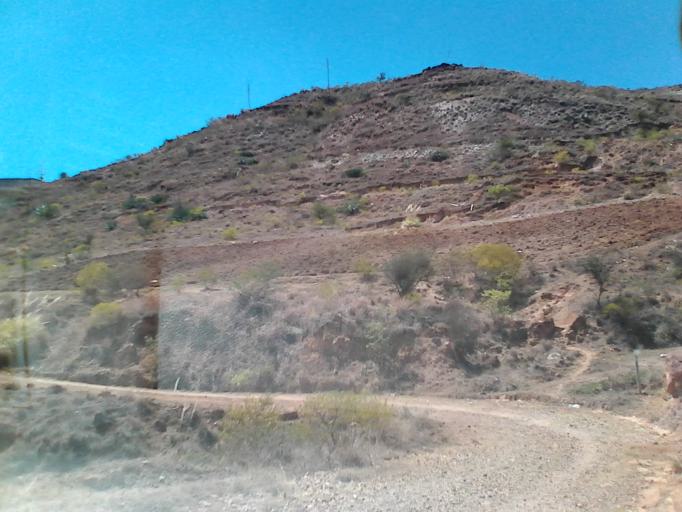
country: CO
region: Boyaca
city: Sachica
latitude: 5.5998
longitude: -73.5735
